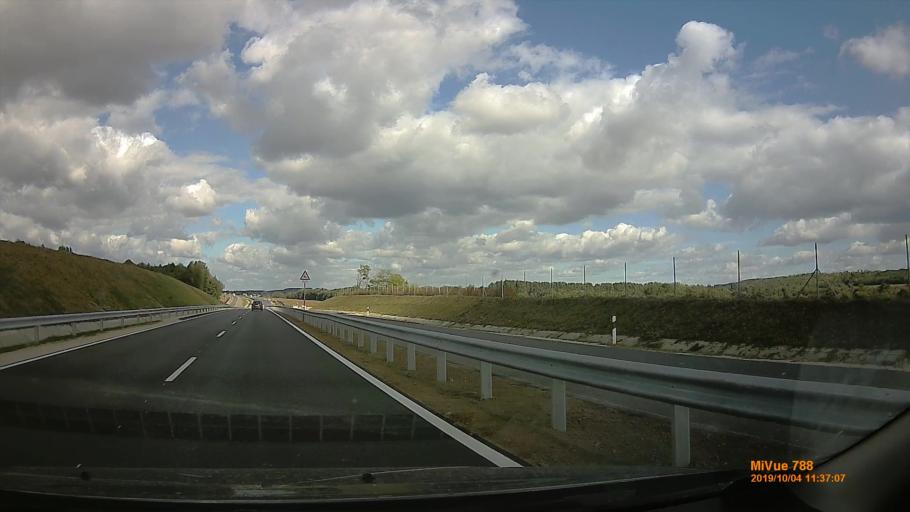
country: HU
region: Somogy
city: Karad
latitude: 46.5321
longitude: 17.8171
